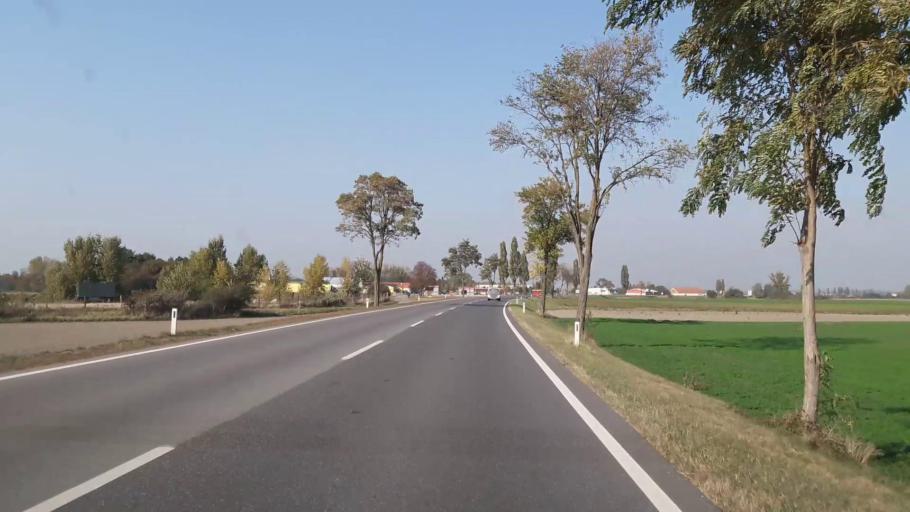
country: AT
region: Lower Austria
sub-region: Politischer Bezirk Ganserndorf
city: Engelhartstetten
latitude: 48.1725
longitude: 16.8918
